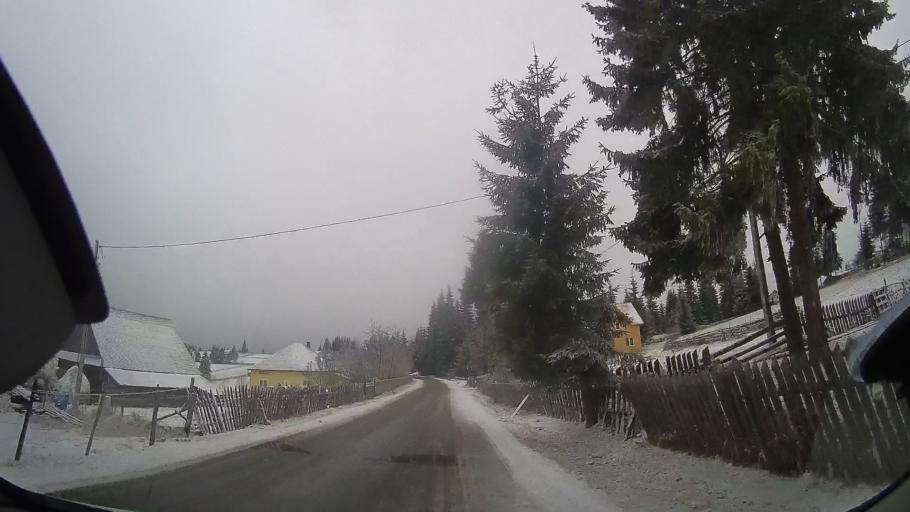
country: RO
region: Cluj
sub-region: Comuna Maguri-Racatau
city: Maguri
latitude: 46.6577
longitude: 23.0884
